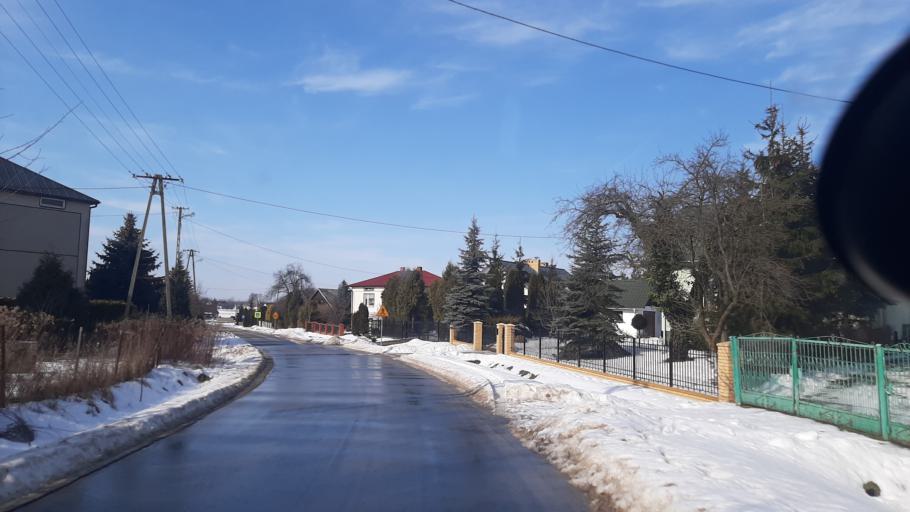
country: PL
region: Lublin Voivodeship
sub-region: Powiat pulawski
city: Baranow
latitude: 51.5373
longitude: 22.1534
